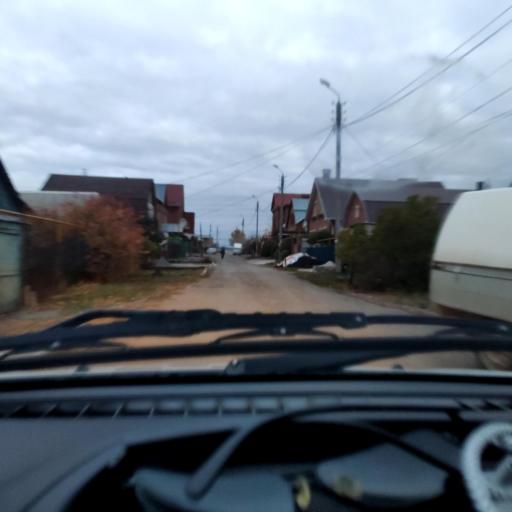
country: RU
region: Samara
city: Zhigulevsk
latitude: 53.4810
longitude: 49.5265
